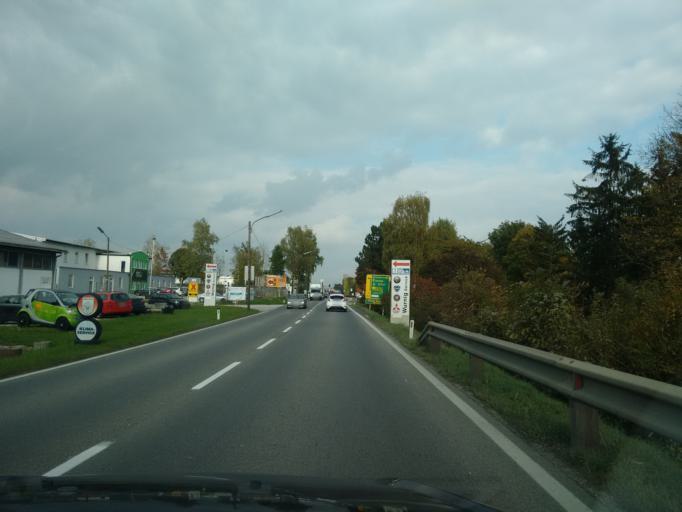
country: AT
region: Upper Austria
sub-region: Wels-Land
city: Gunskirchen
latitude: 48.1413
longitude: 13.9700
